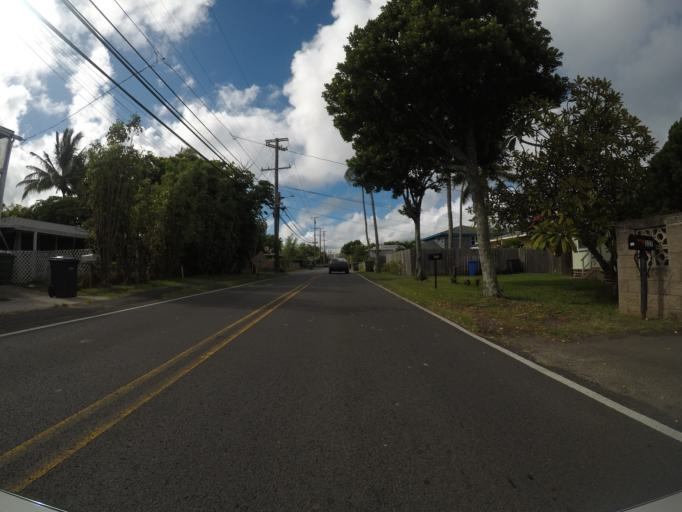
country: US
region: Hawaii
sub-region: Honolulu County
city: Kailua
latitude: 21.4011
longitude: -157.7438
